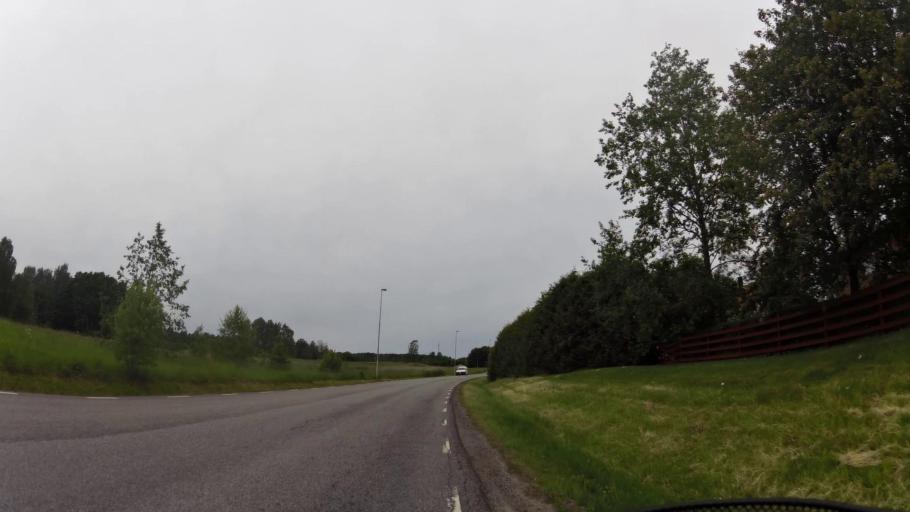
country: SE
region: OEstergoetland
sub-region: Linkopings Kommun
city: Malmslatt
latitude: 58.3887
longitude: 15.5546
